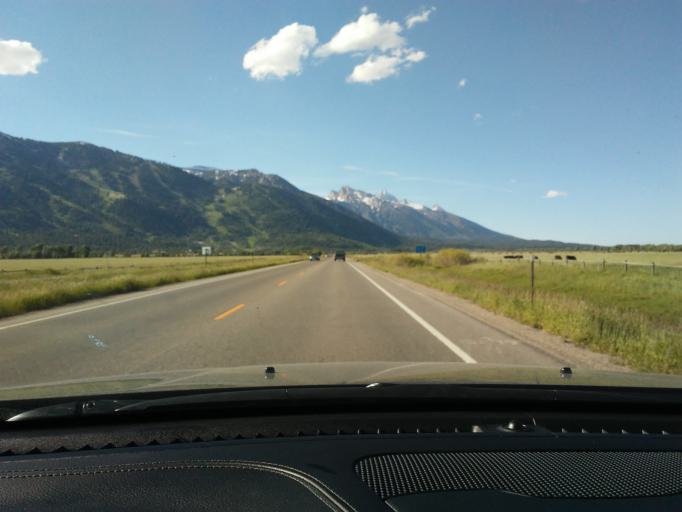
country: US
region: Wyoming
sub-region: Teton County
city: Moose Wilson Road
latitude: 43.5617
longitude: -110.8220
